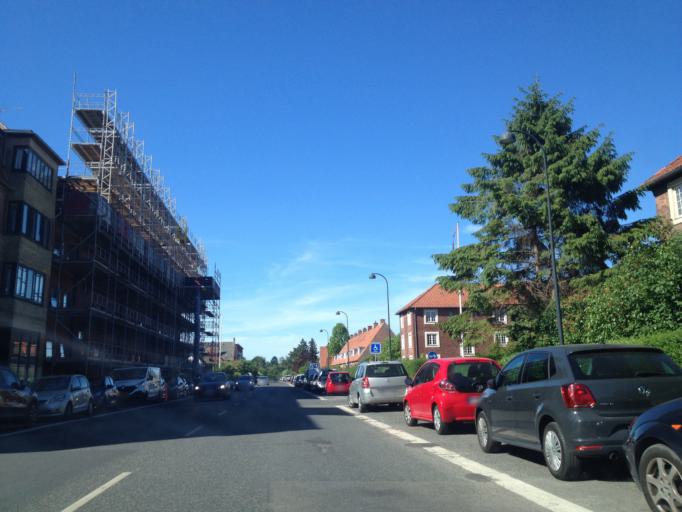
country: DK
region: Capital Region
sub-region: Gentofte Kommune
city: Charlottenlund
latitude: 55.7622
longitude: 12.5859
